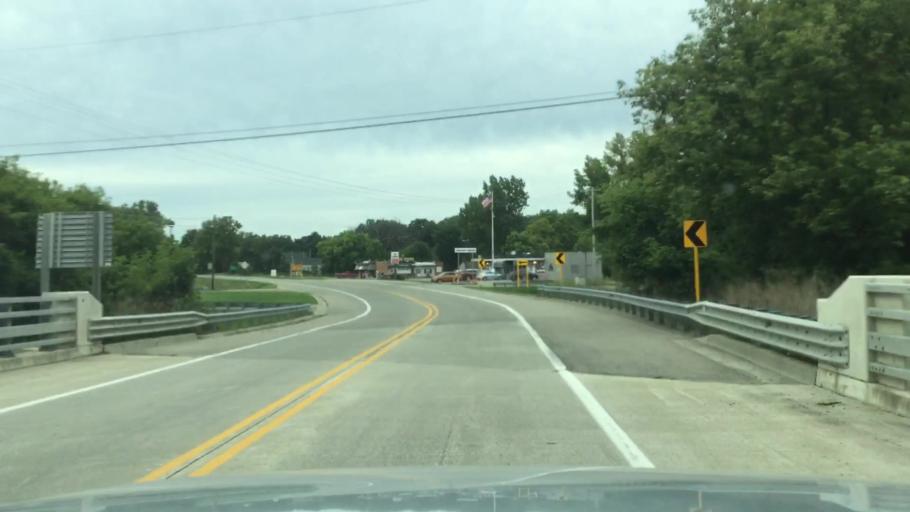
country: US
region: Michigan
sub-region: Shiawassee County
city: Durand
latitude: 42.9290
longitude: -84.0026
